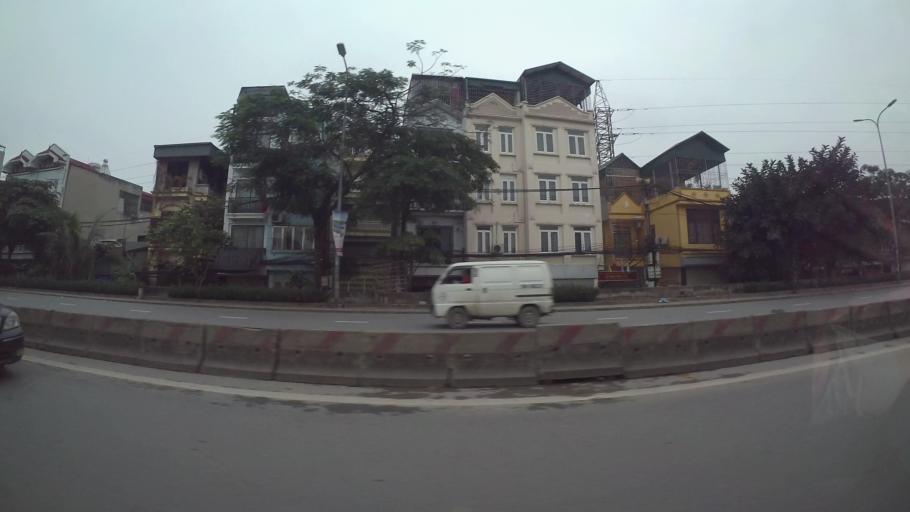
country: VN
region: Ha Noi
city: Hai BaTrung
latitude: 21.0069
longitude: 105.8676
